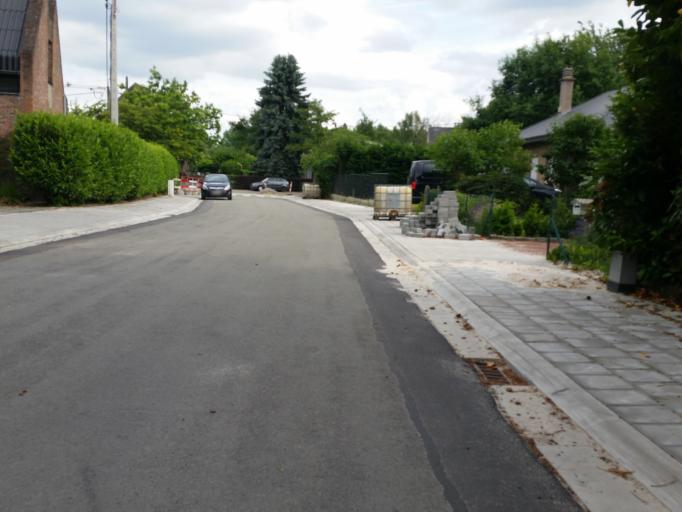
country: BE
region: Flanders
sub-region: Provincie Antwerpen
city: Mechelen
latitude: 50.9996
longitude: 4.4896
